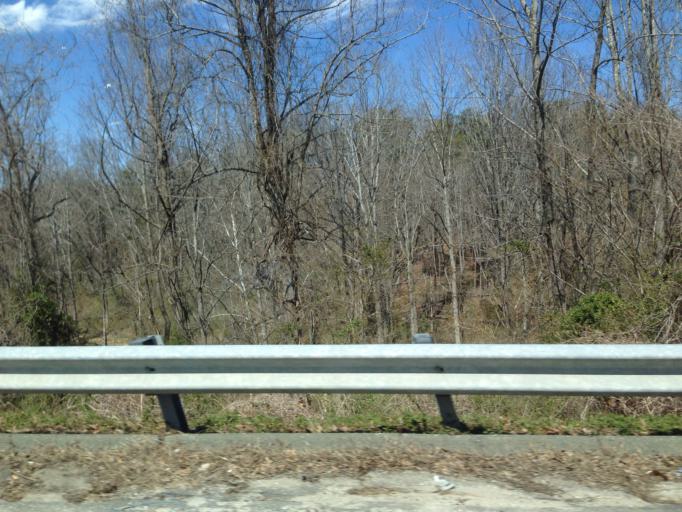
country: US
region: Virginia
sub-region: City of Charlottesville
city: Charlottesville
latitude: 38.0222
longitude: -78.5384
